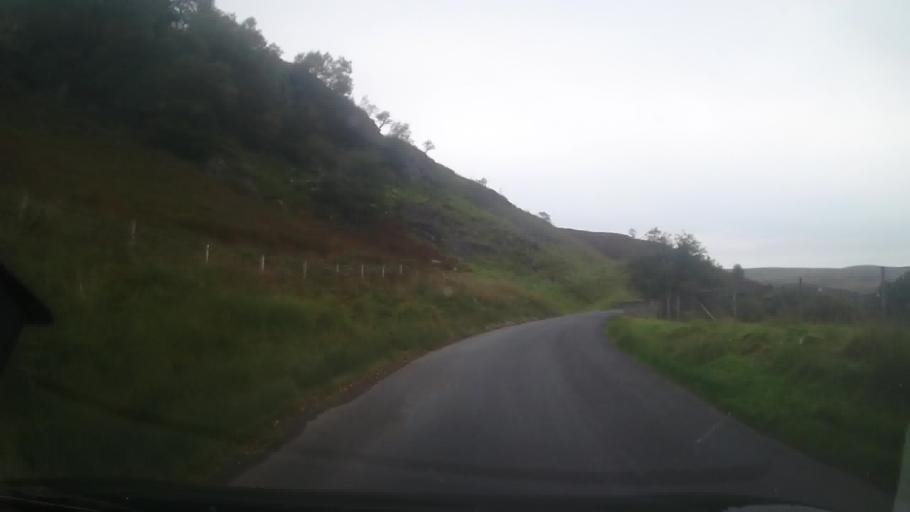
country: GB
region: Wales
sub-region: Sir Powys
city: Rhayader
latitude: 52.2994
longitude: -3.6219
